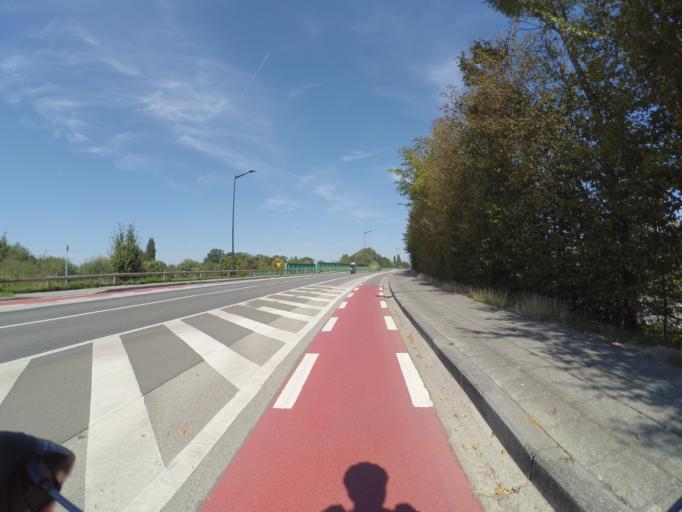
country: BE
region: Flanders
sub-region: Provincie Oost-Vlaanderen
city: Oudenaarde
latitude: 50.8383
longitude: 3.6041
